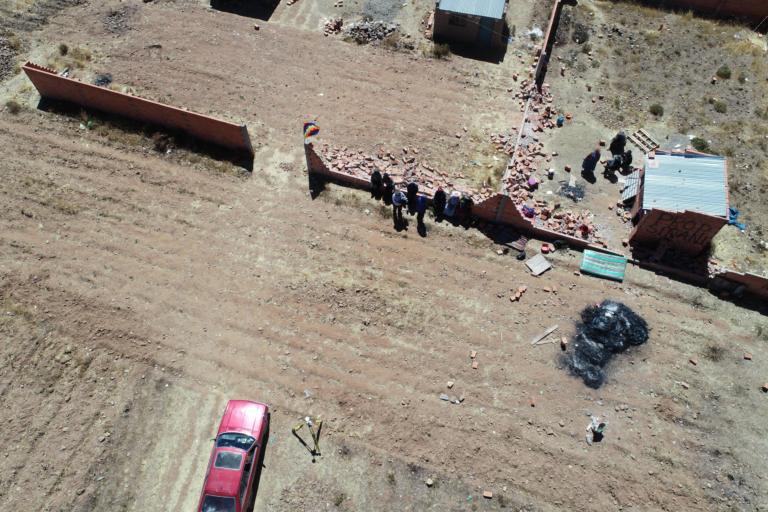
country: BO
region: La Paz
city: La Paz
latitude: -16.4672
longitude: -68.2963
